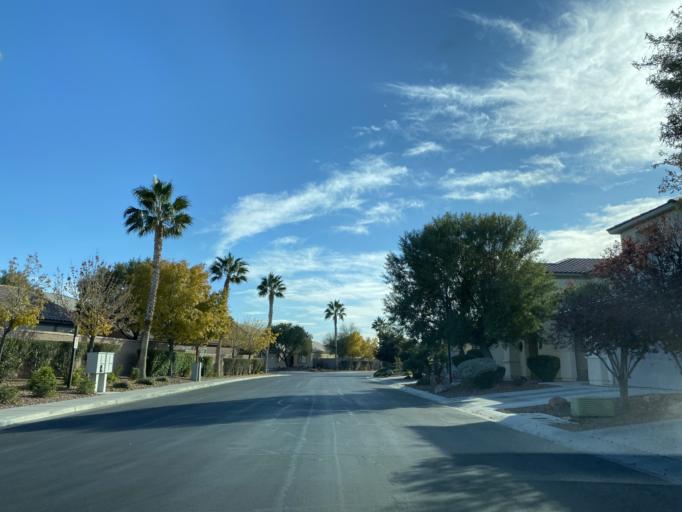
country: US
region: Nevada
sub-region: Clark County
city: North Las Vegas
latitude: 36.3192
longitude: -115.2431
